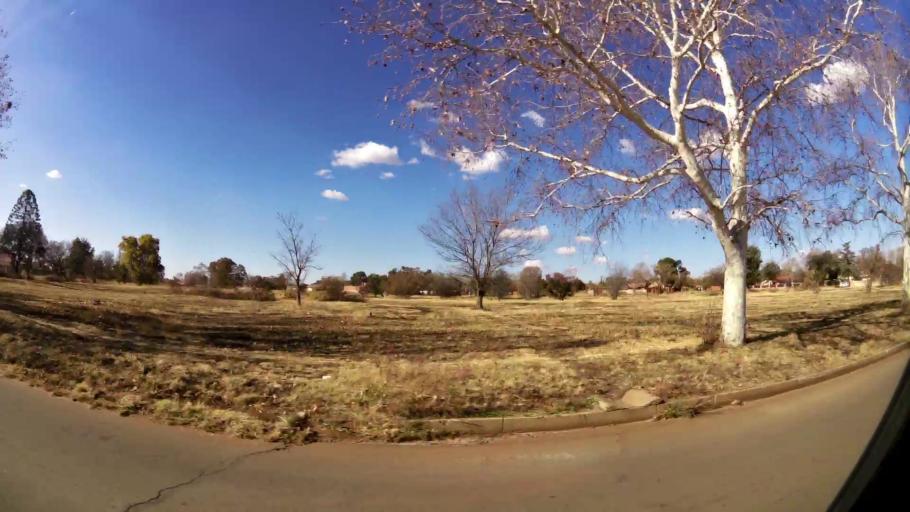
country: ZA
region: Gauteng
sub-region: West Rand District Municipality
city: Carletonville
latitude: -26.3718
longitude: 27.3965
